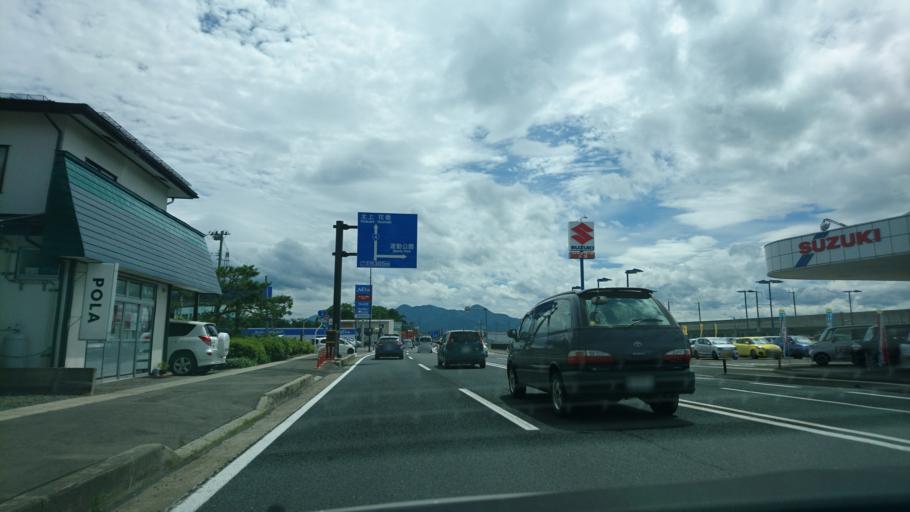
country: JP
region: Iwate
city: Morioka-shi
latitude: 39.7408
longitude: 141.1283
